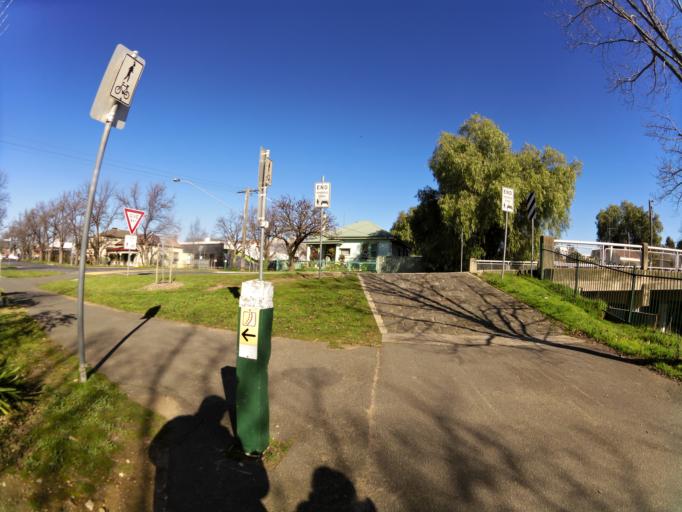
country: AU
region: Victoria
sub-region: Greater Bendigo
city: Bendigo
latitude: -36.7530
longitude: 144.2851
